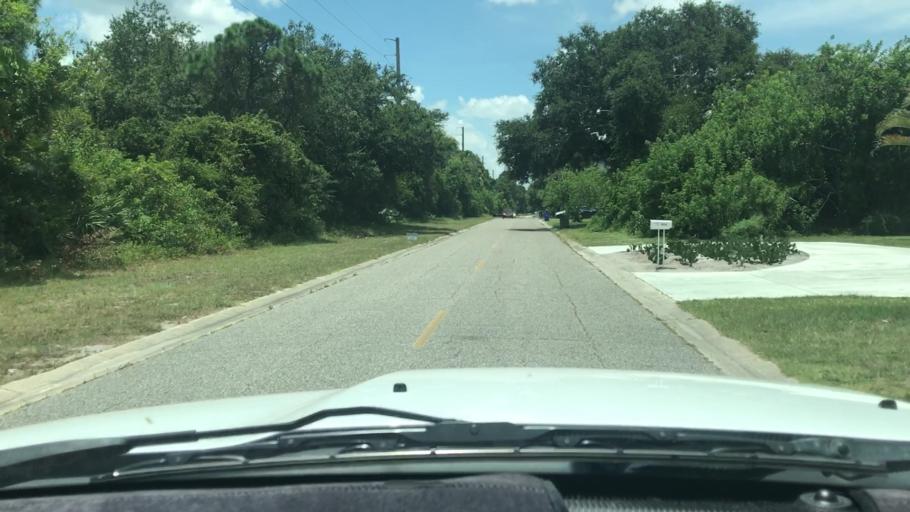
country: US
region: Florida
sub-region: Saint Lucie County
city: Lakewood Park
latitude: 27.5580
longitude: -80.3946
